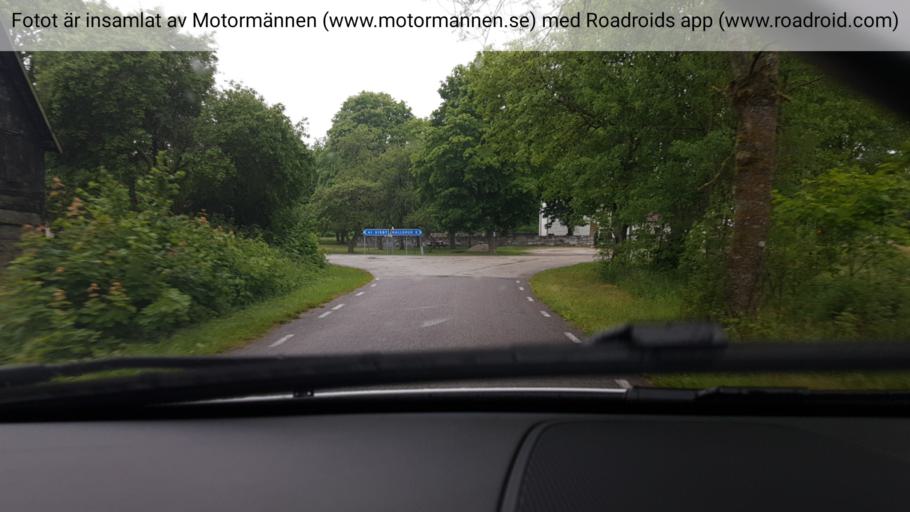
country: SE
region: Gotland
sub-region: Gotland
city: Slite
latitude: 57.8919
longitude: 18.7177
